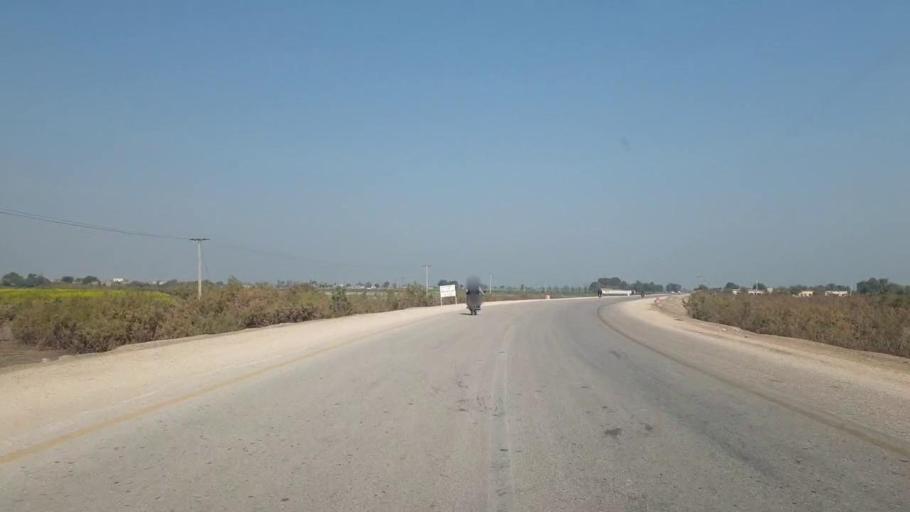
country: PK
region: Sindh
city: Sakrand
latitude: 26.0139
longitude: 68.3937
